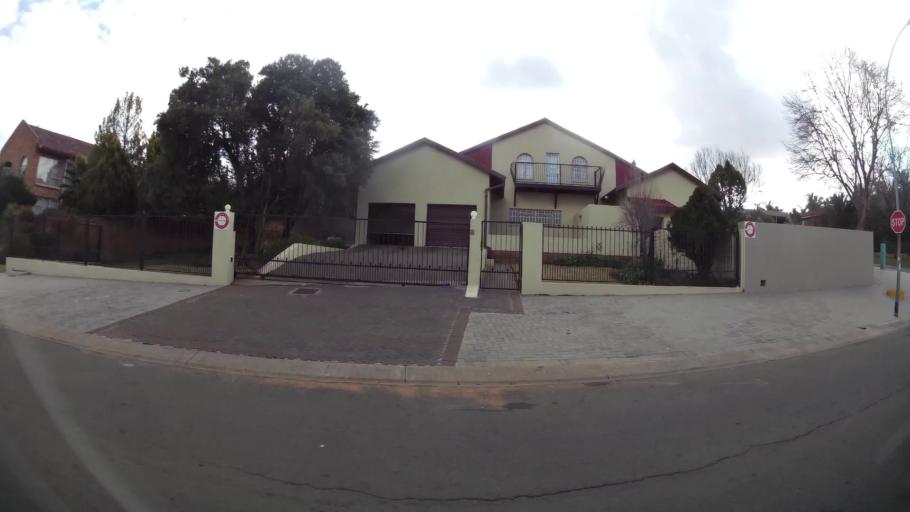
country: ZA
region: Orange Free State
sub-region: Mangaung Metropolitan Municipality
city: Bloemfontein
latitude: -29.0856
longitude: 26.2018
